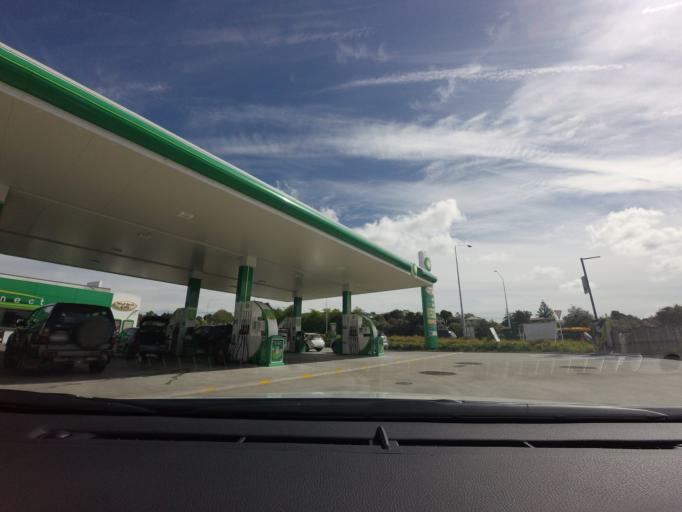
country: NZ
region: Auckland
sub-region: Auckland
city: Warkworth
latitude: -36.4086
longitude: 174.6594
